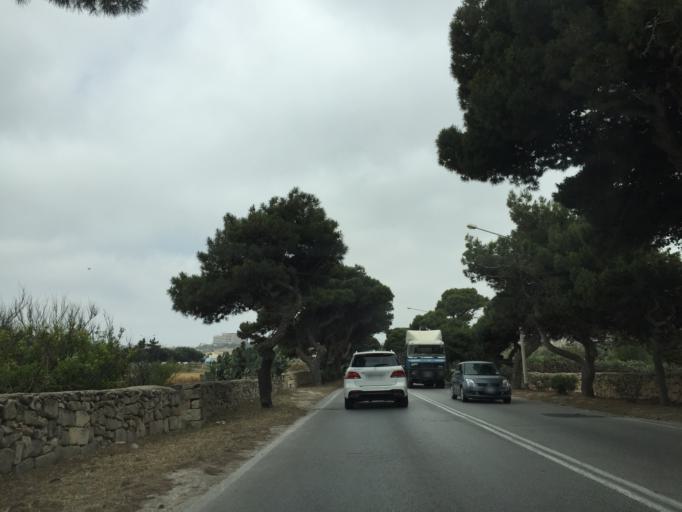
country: MT
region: L-Imdina
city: Imdina
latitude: 35.8841
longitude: 14.4179
